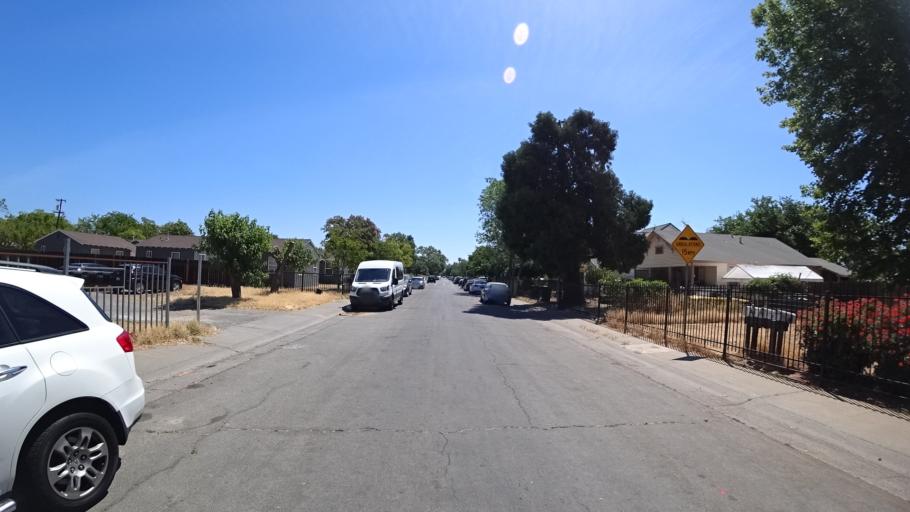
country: US
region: California
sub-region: Sacramento County
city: Parkway
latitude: 38.5182
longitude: -121.4755
